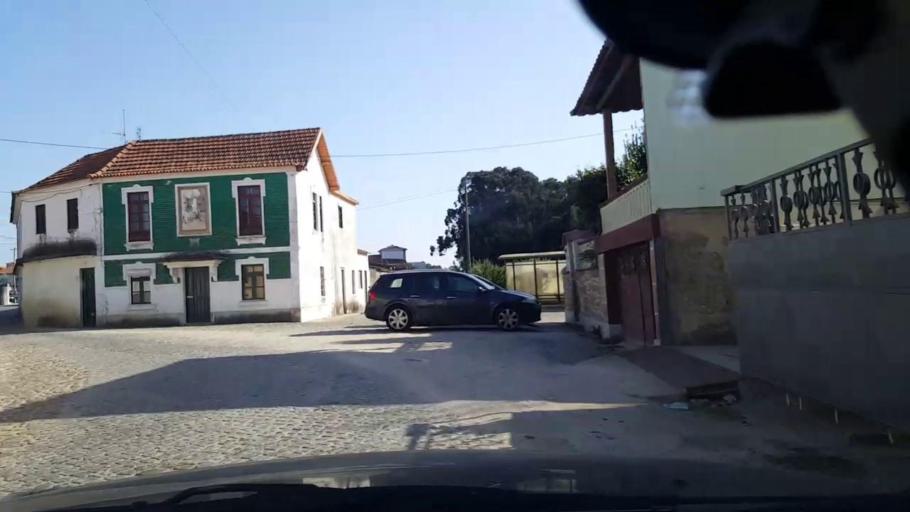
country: PT
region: Porto
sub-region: Vila do Conde
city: Arvore
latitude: 41.3536
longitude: -8.7216
